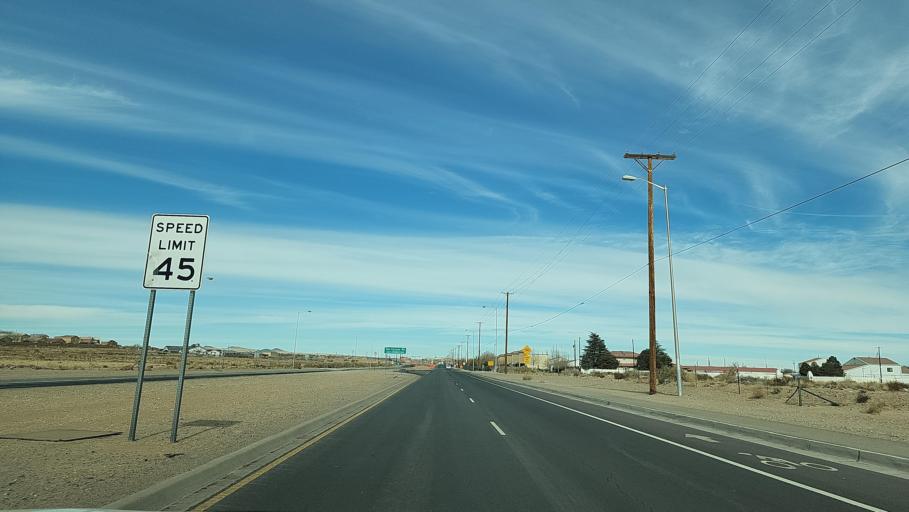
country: US
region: New Mexico
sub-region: Bernalillo County
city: South Valley
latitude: 35.0618
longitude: -106.7084
